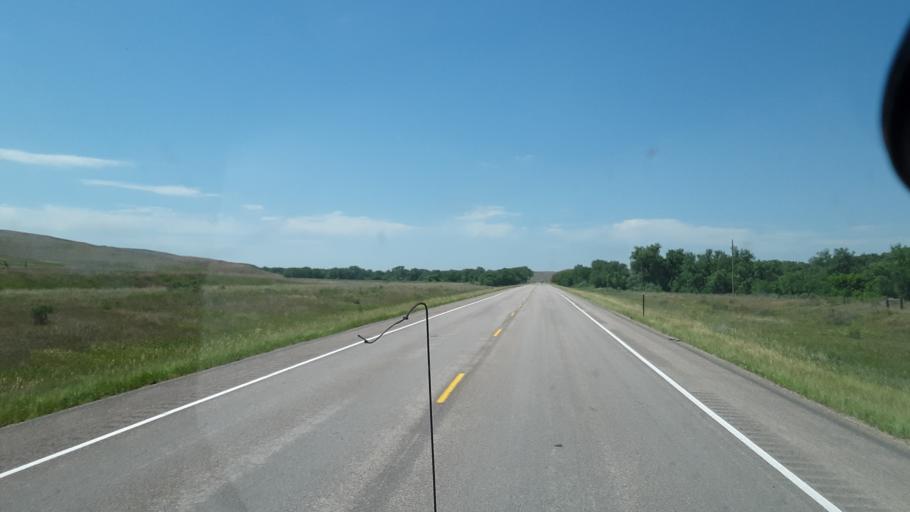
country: US
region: South Dakota
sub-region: Pennington County
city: Box Elder
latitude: 43.9104
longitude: -102.6959
